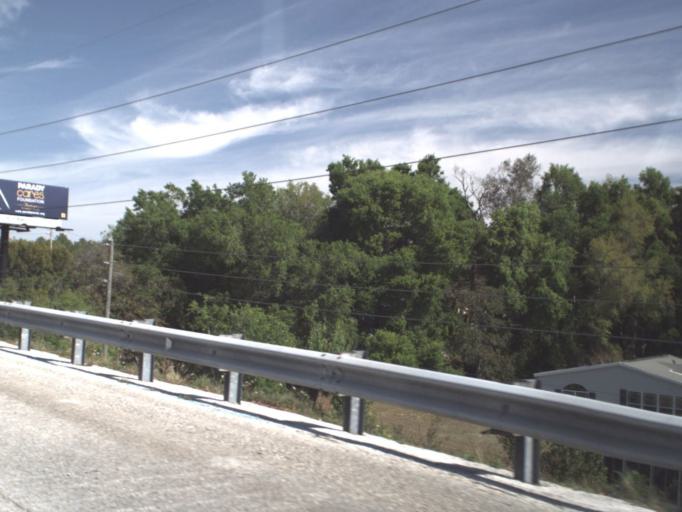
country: US
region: Florida
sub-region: Lake County
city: Lady Lake
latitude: 28.9280
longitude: -81.9255
